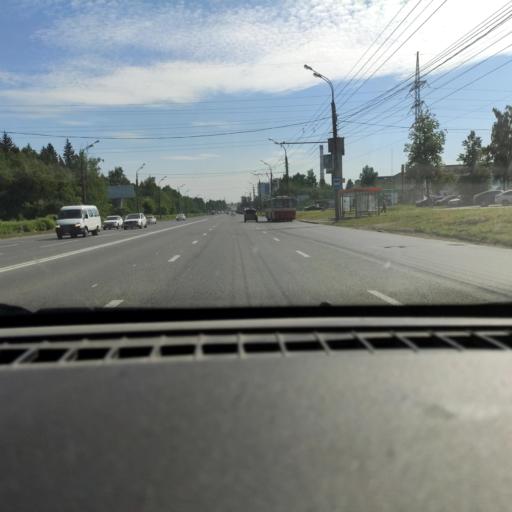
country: RU
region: Udmurtiya
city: Khokhryaki
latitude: 56.8931
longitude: 53.2706
